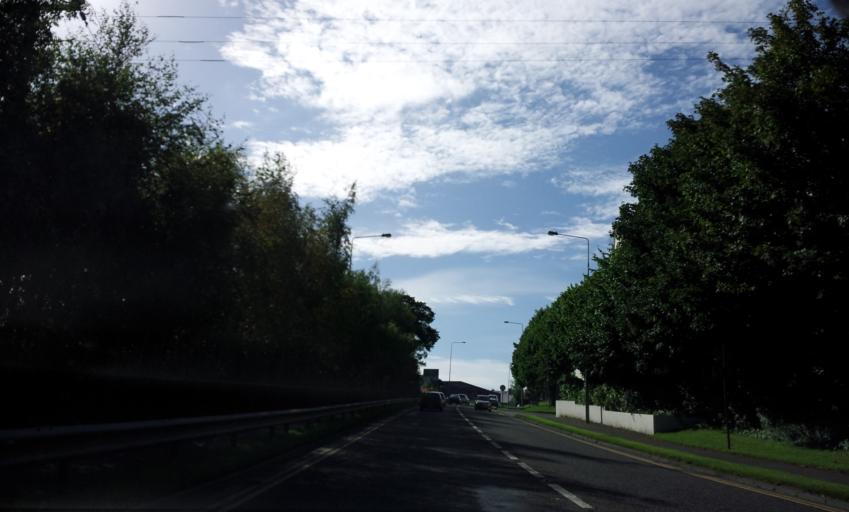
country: IE
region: Munster
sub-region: Ciarrai
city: Cill Airne
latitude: 52.0588
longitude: -9.4780
